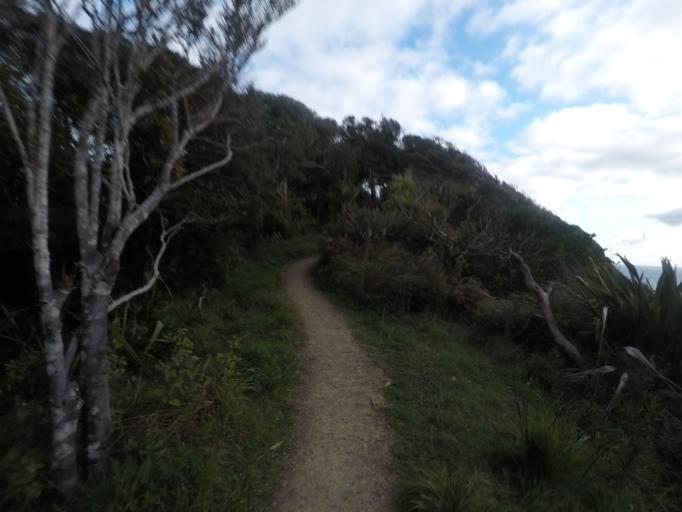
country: NZ
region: Auckland
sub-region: Auckland
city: Muriwai Beach
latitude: -36.9782
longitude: 174.4727
